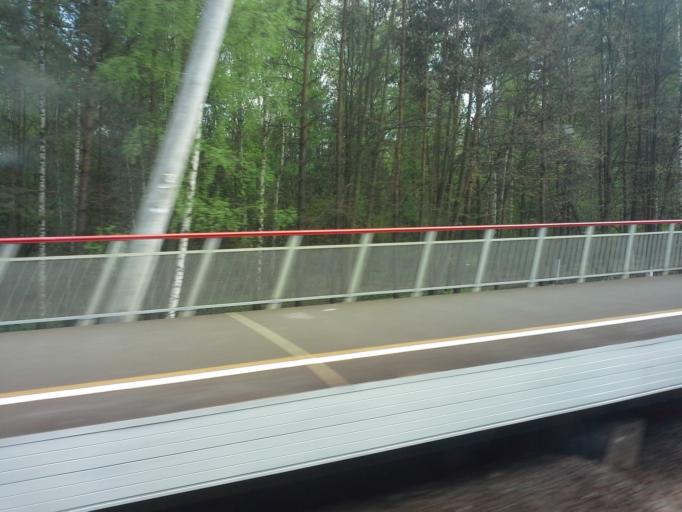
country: RU
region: Moskovskaya
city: Zelenogradskiy
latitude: 56.0949
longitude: 37.9014
